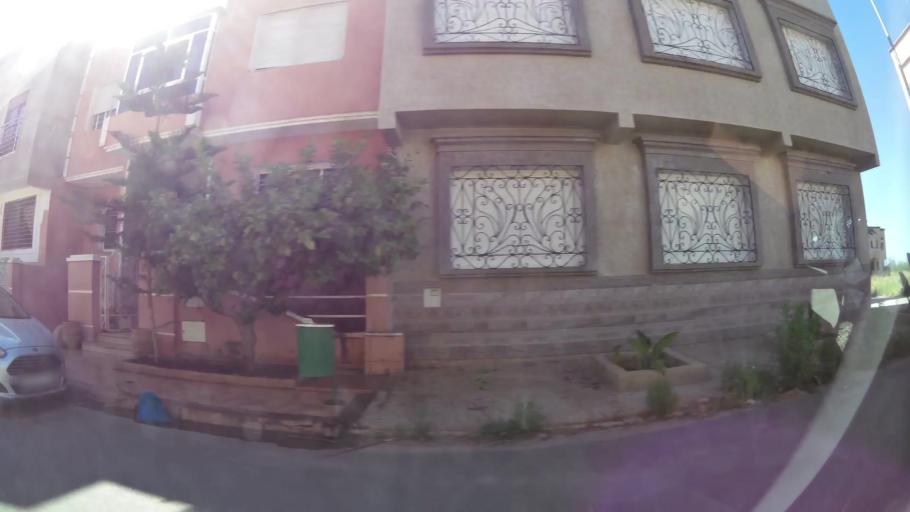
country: MA
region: Oriental
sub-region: Berkane-Taourirt
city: Berkane
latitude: 34.9465
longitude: -2.3348
